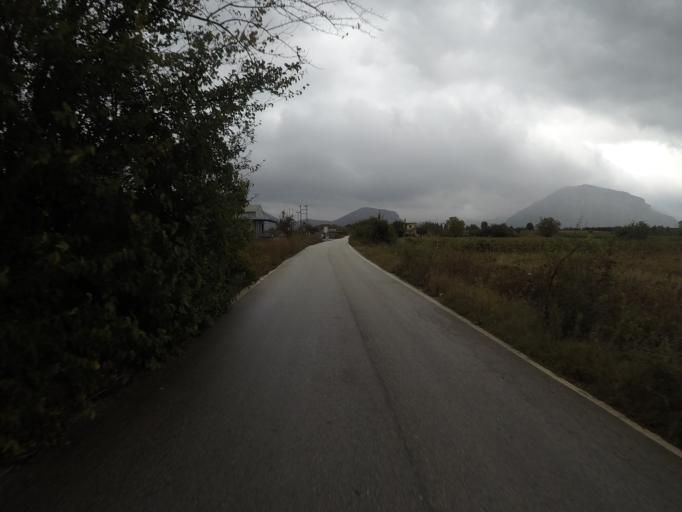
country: GR
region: Peloponnese
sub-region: Nomos Arkadias
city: Tripoli
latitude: 37.5728
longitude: 22.4113
